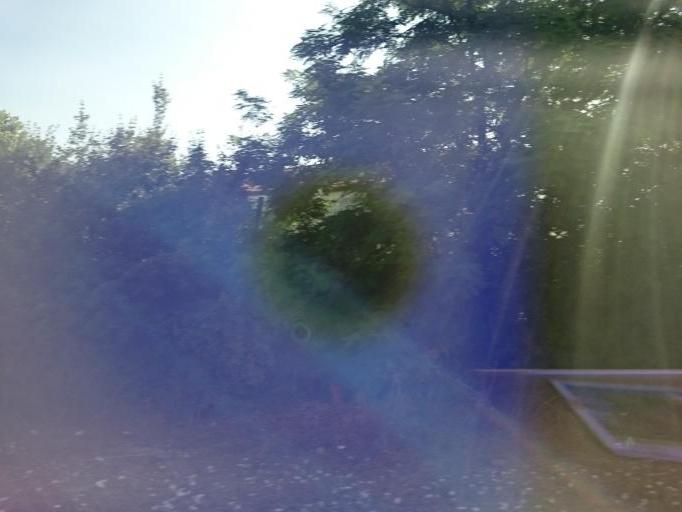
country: IT
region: Veneto
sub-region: Provincia di Verona
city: Sant'Ambrogio di Valpollicella
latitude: 45.5105
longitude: 10.8291
